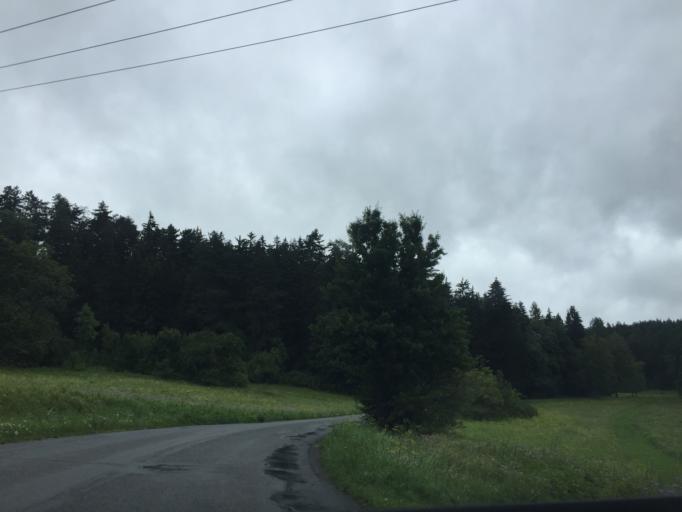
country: CZ
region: South Moravian
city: Ostrov u Macochy
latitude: 49.3844
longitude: 16.7656
